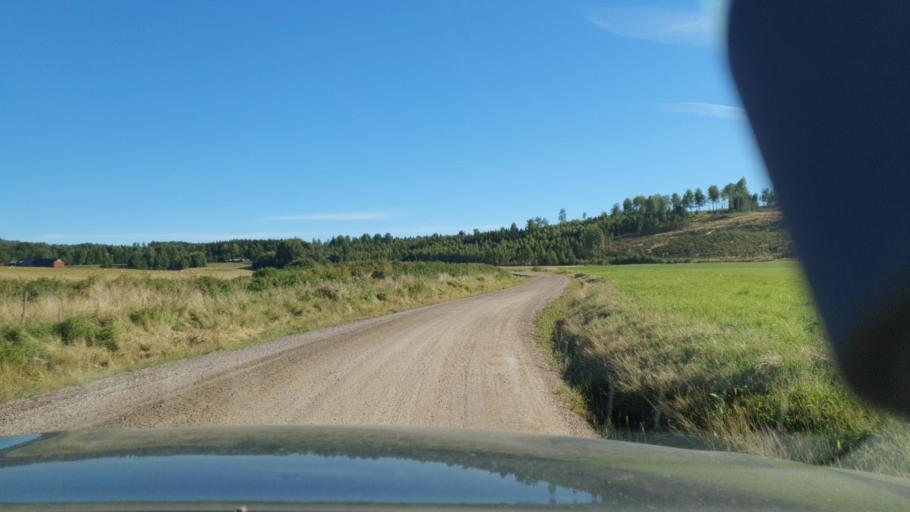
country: SE
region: Vaermland
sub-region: Karlstads Kommun
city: Molkom
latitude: 59.5495
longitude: 13.8462
